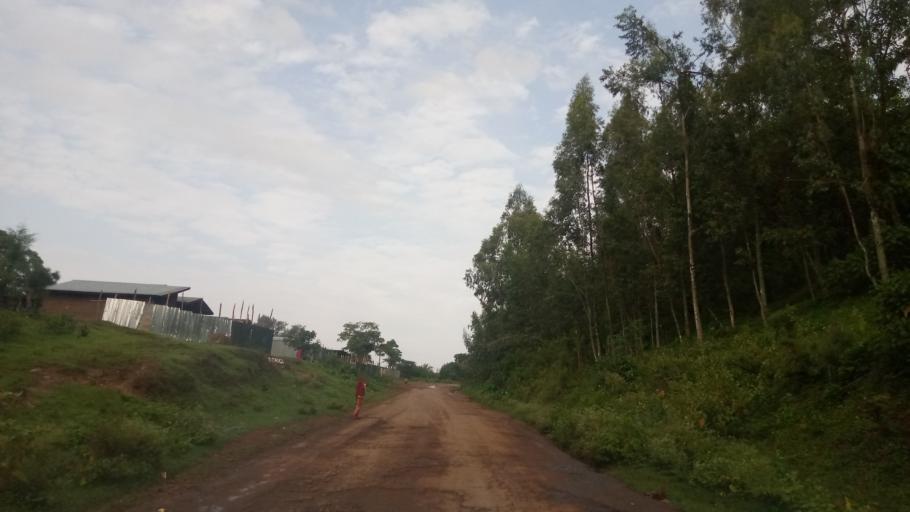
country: ET
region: Oromiya
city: Agaro
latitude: 7.8366
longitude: 36.6751
